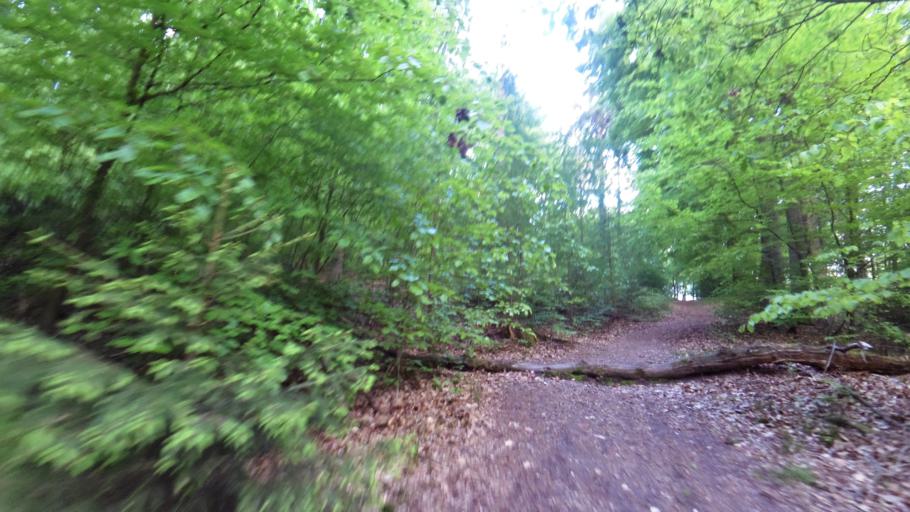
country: NL
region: Gelderland
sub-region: Gemeente Rozendaal
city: Rozendaal
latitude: 52.0122
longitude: 5.9637
